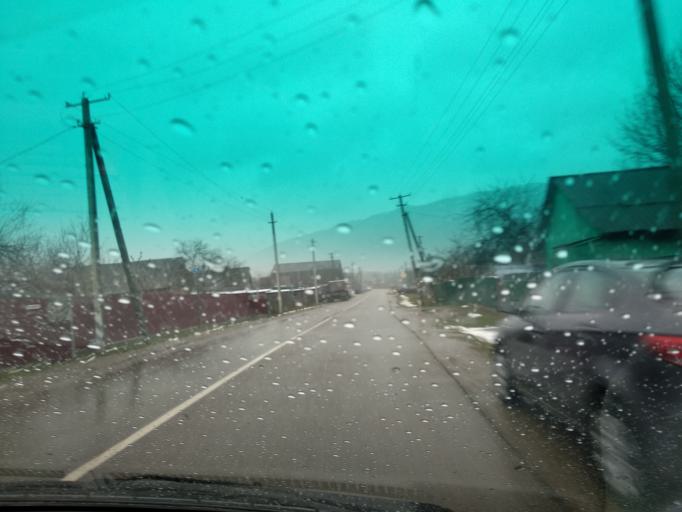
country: RU
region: Krasnodarskiy
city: Khadyzhensk
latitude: 44.2525
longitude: 39.3683
